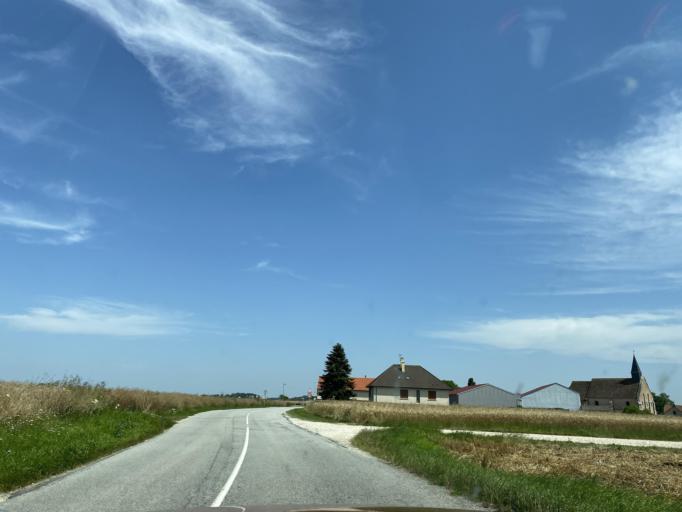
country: FR
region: Centre
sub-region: Departement d'Eure-et-Loir
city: Le Coudray
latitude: 48.4093
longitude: 1.5252
